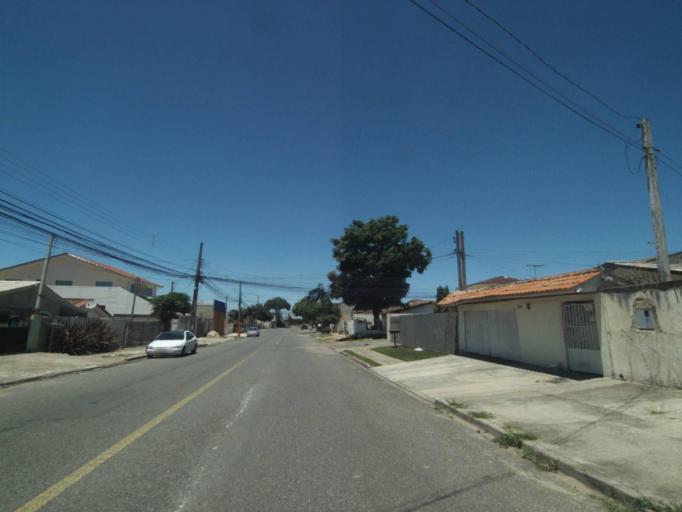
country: BR
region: Parana
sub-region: Curitiba
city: Curitiba
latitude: -25.4785
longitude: -49.3474
